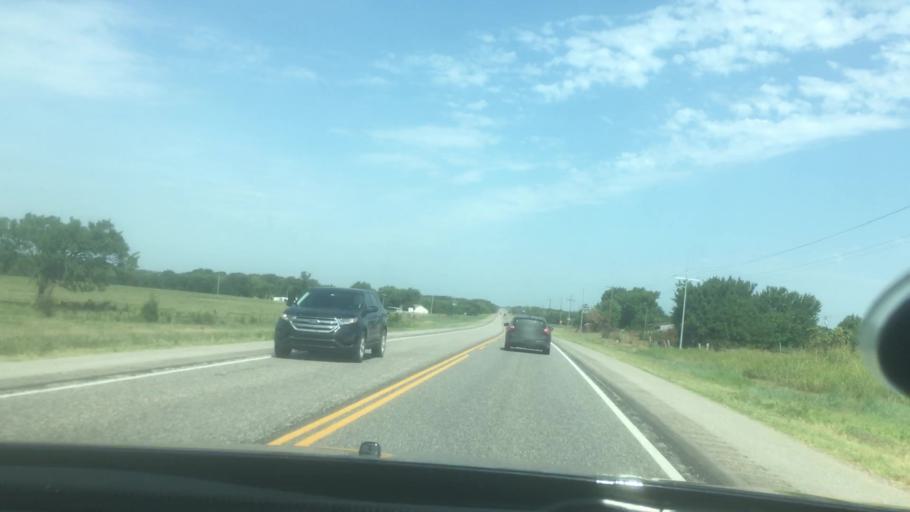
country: US
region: Oklahoma
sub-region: Seminole County
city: Konawa
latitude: 34.8675
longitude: -96.8350
